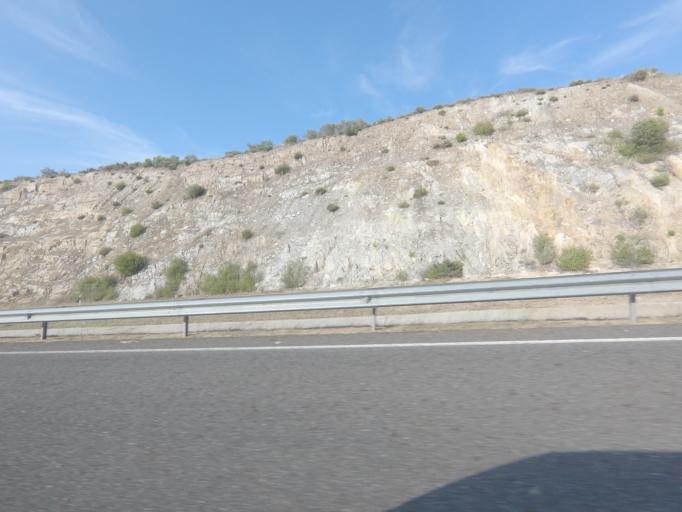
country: ES
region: Galicia
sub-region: Provincia de Ourense
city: Oimbra
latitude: 41.8598
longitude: -7.4256
